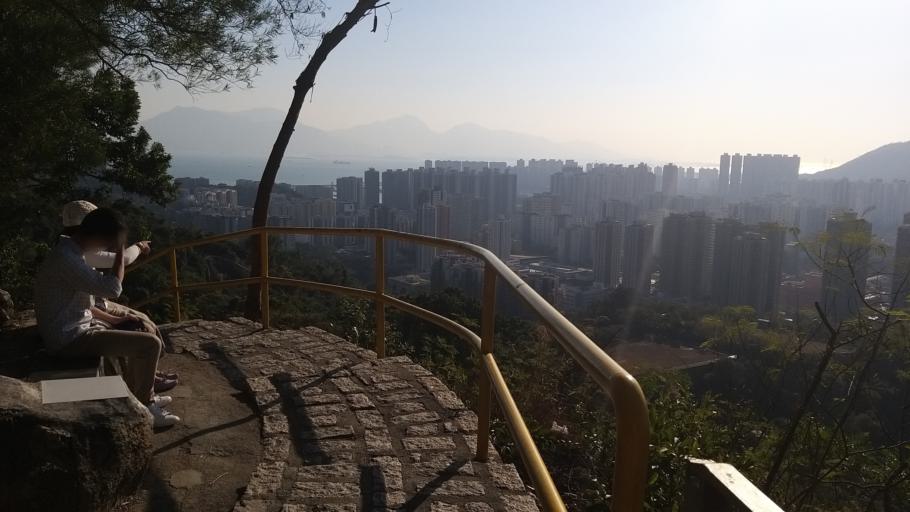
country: HK
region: Tuen Mun
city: Tuen Mun
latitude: 22.3960
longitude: 113.9830
